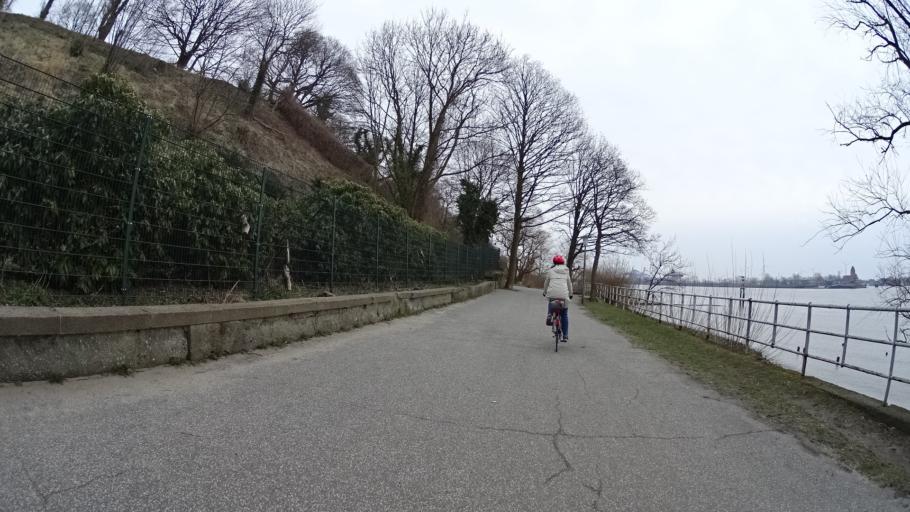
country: DE
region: Hamburg
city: Altona
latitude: 53.5463
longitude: 9.8730
